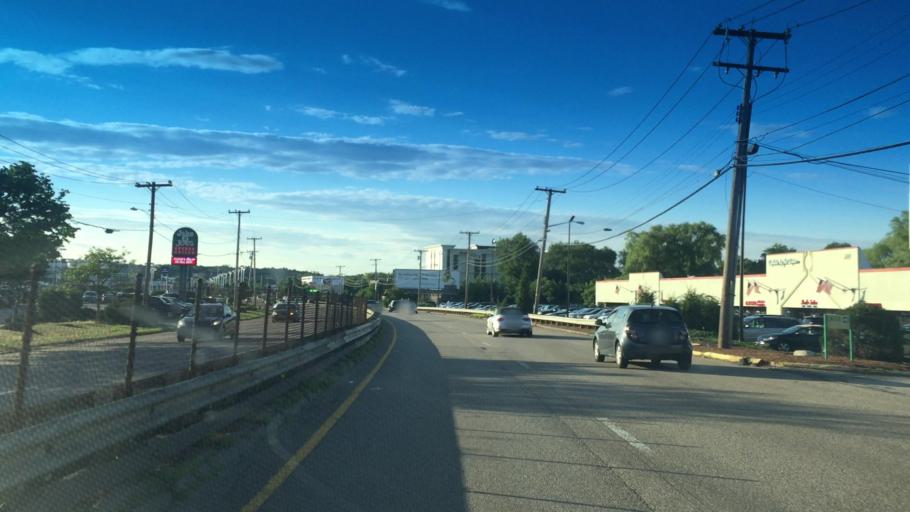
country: US
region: Massachusetts
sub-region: Norfolk County
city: Norwood
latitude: 42.1944
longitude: -71.1838
